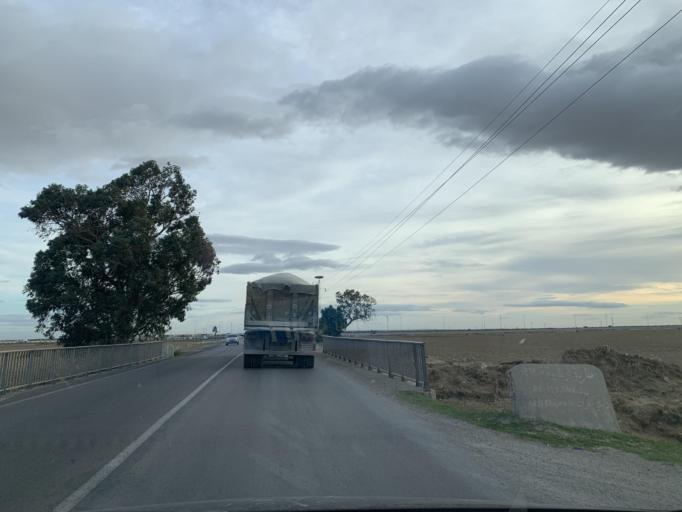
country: TN
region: Susah
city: Harqalah
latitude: 36.1050
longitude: 10.3878
